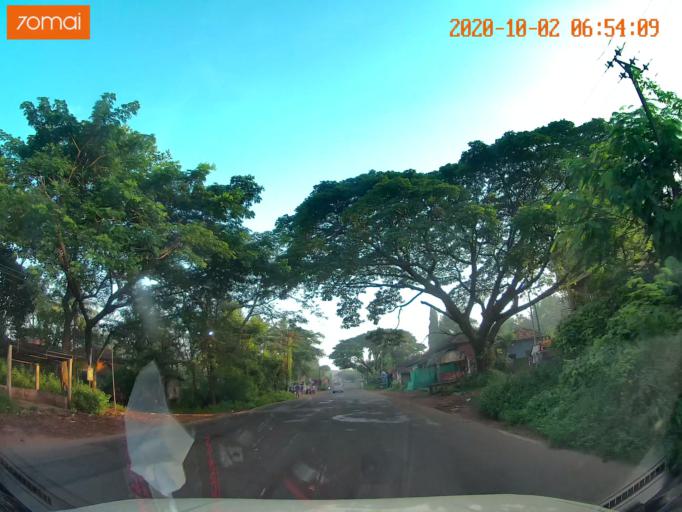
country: IN
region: Kerala
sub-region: Malappuram
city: Tirur
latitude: 10.8544
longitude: 76.0365
